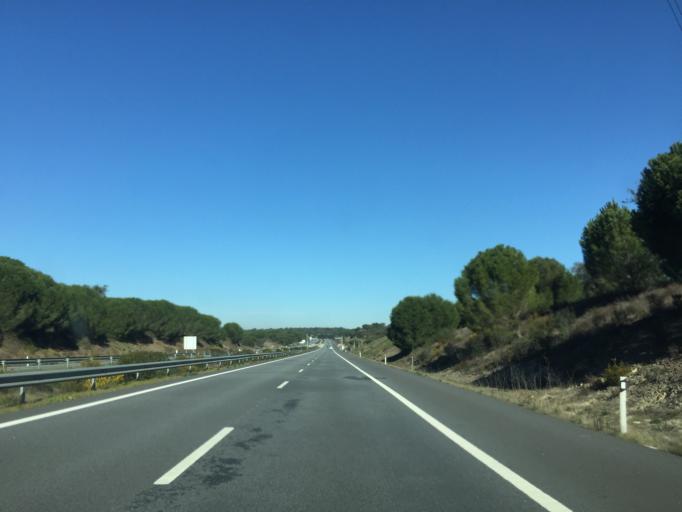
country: PT
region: Evora
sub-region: Vendas Novas
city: Vendas Novas
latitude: 38.5740
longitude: -8.6197
